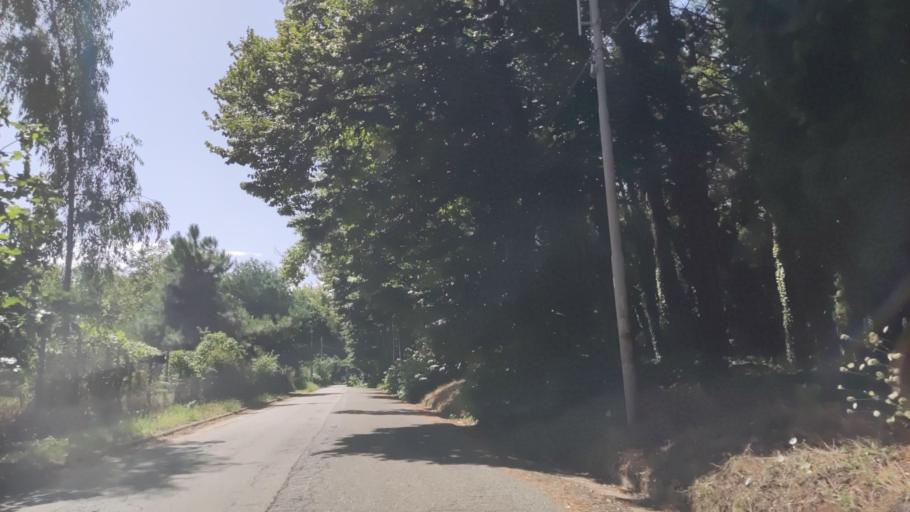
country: IT
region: Calabria
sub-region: Provincia di Reggio Calabria
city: Seminara
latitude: 38.3415
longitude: 15.8444
